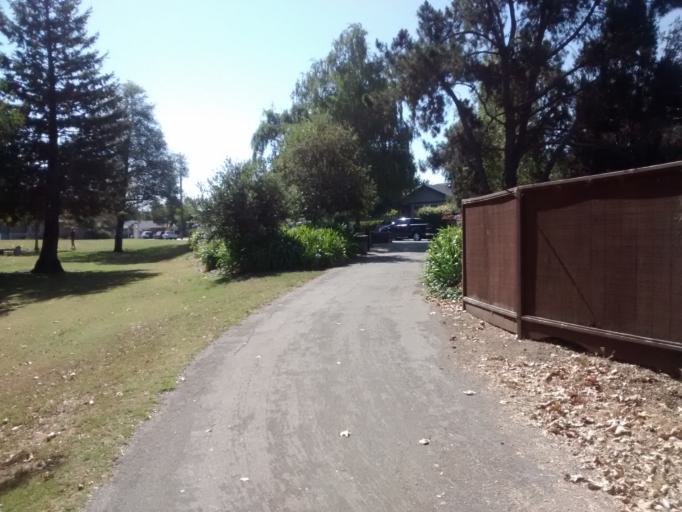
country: US
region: California
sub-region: San Luis Obispo County
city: San Luis Obispo
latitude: 35.2675
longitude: -120.6591
